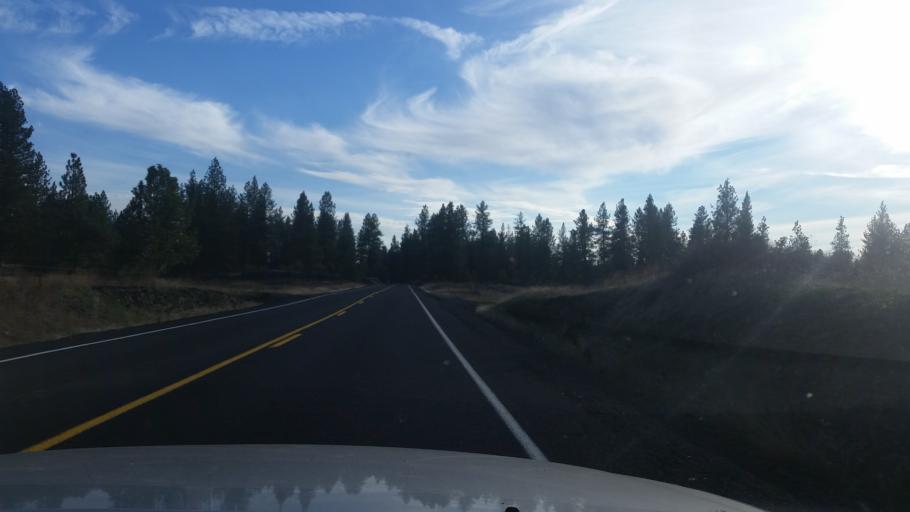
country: US
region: Washington
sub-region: Spokane County
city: Cheney
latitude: 47.4471
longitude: -117.5756
